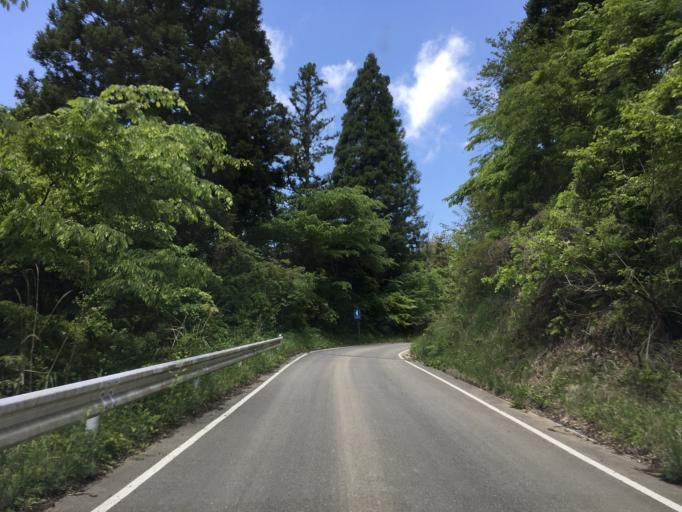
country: JP
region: Miyagi
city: Wakuya
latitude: 38.6887
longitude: 141.3481
